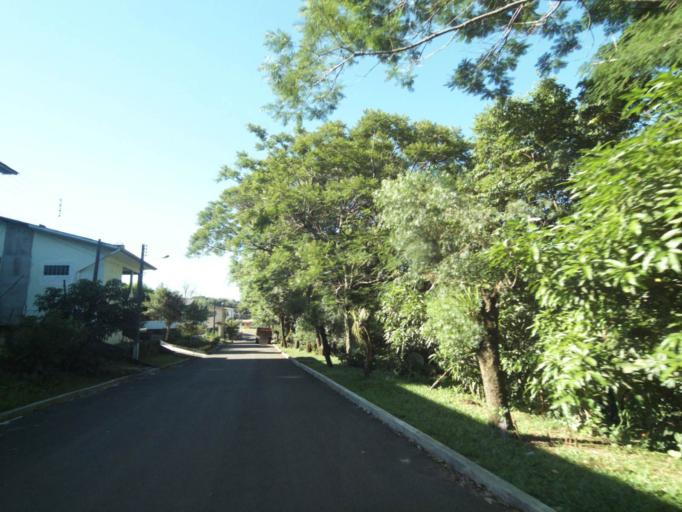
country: BR
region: Parana
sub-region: Ampere
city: Ampere
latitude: -26.1742
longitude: -53.3634
